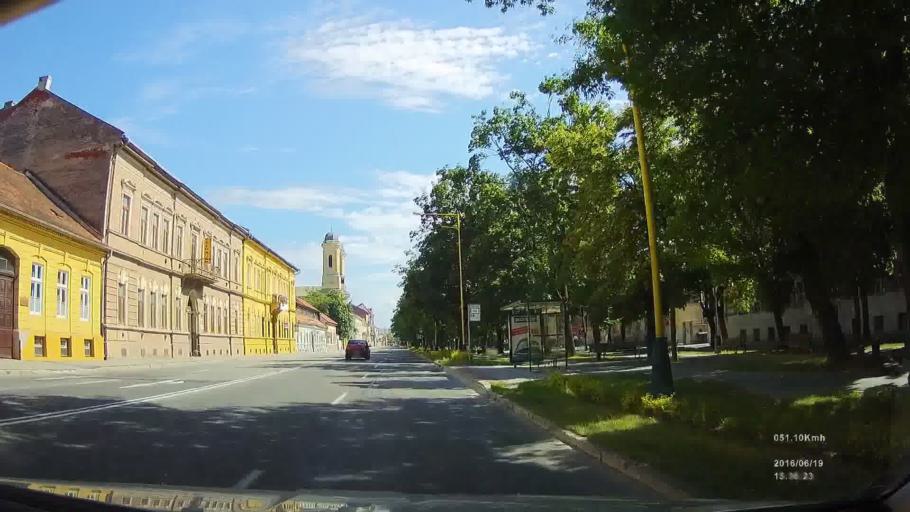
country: SK
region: Kosicky
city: Kosice
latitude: 48.7220
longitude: 21.2520
